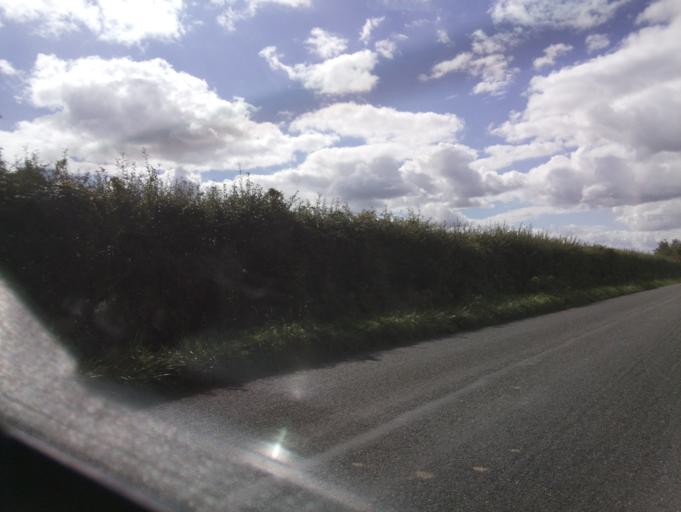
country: GB
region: England
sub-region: Wiltshire
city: Melksham
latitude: 51.3225
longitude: -2.1559
